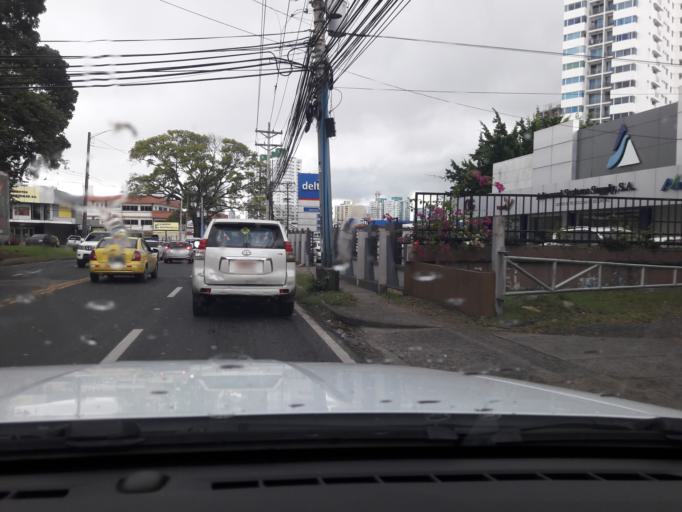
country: PA
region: Panama
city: Panama
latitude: 9.0051
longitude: -79.5112
